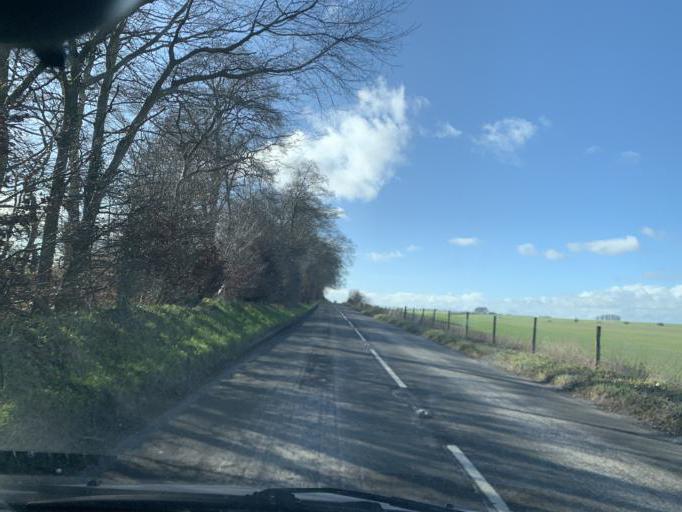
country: GB
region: England
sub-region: Wiltshire
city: Boyton
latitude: 51.1875
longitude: -2.0524
